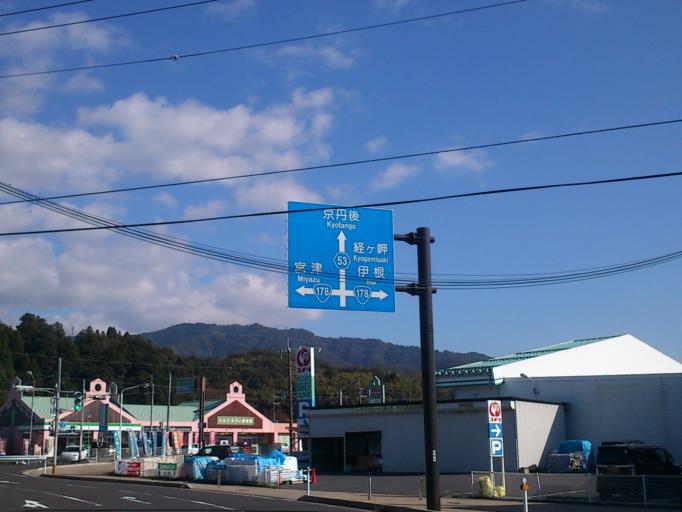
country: JP
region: Kyoto
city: Miyazu
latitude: 35.5709
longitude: 135.1612
